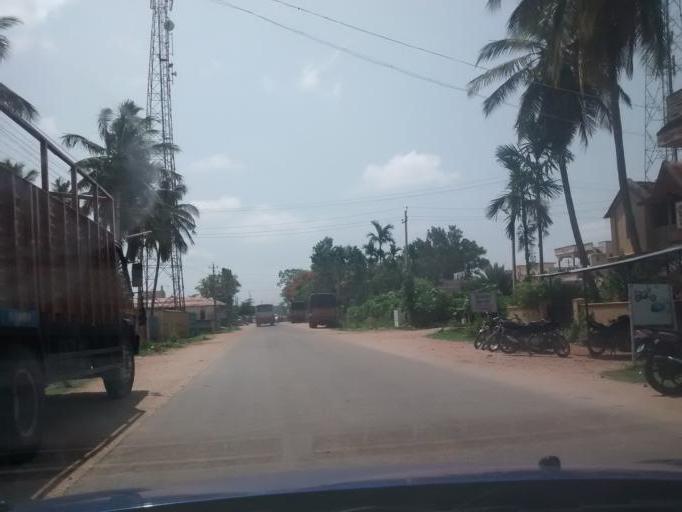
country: IN
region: Karnataka
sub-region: Hassan
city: Konanur
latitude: 12.5632
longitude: 76.2611
